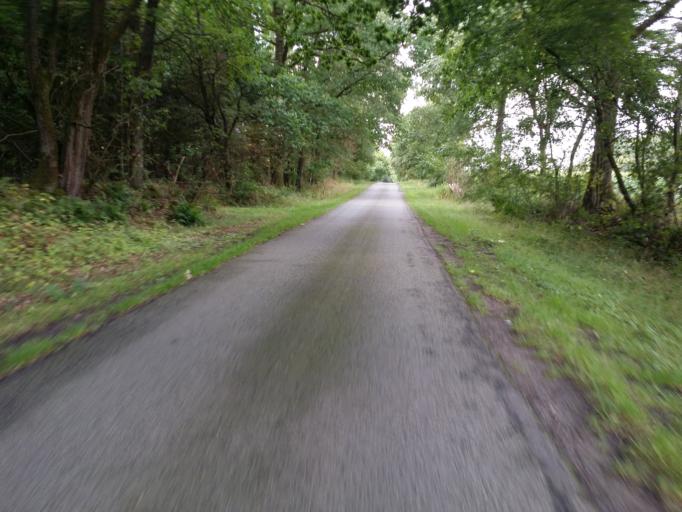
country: DE
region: Schleswig-Holstein
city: Vaale
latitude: 54.0117
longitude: 9.3982
